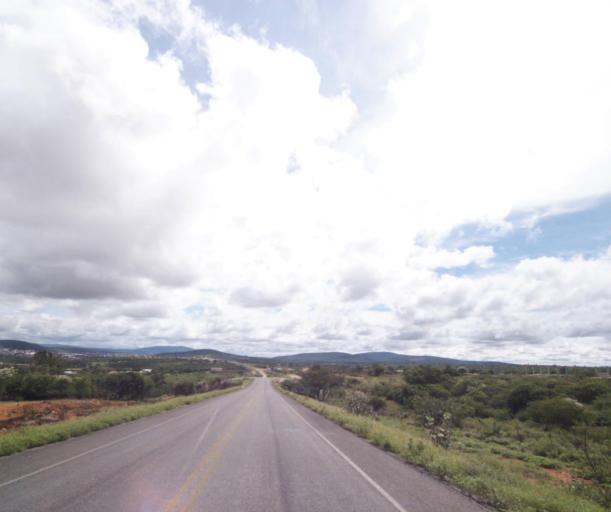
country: BR
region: Bahia
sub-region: Brumado
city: Brumado
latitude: -14.2353
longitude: -41.6881
